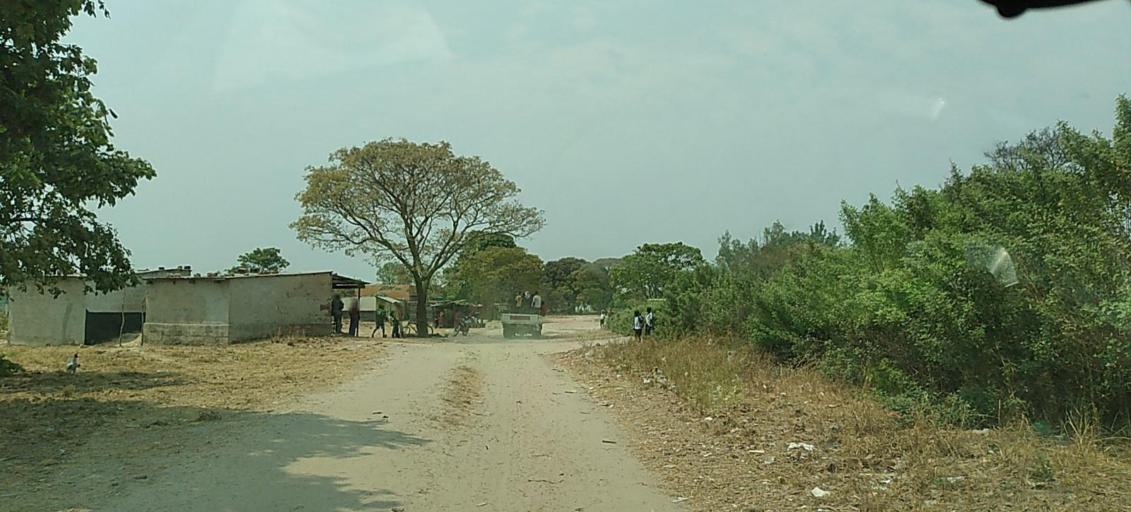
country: ZM
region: North-Western
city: Kabompo
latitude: -13.4937
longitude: 24.4650
